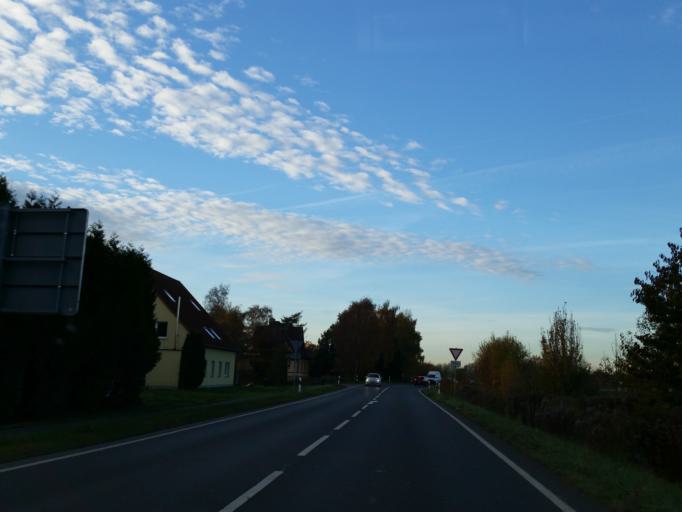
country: DE
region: Lower Saxony
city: Cremlingen
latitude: 52.2488
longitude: 10.5981
